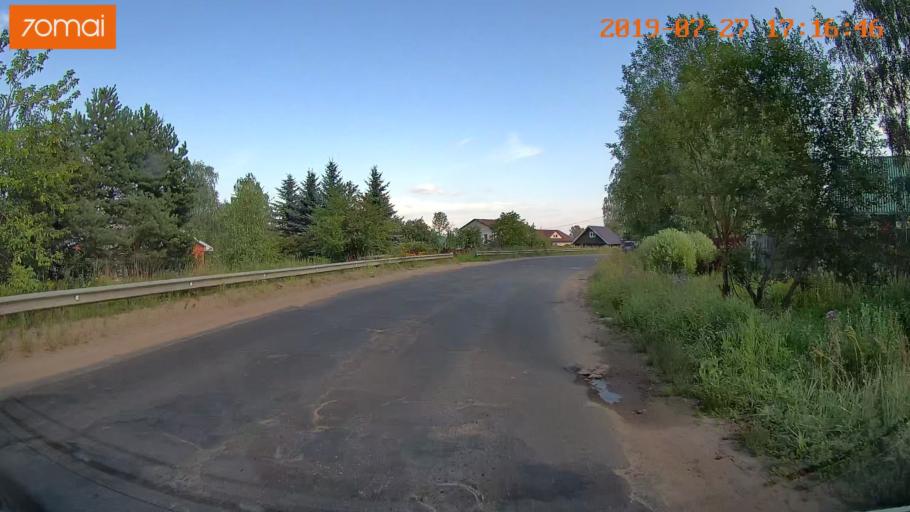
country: RU
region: Ivanovo
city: Novo-Talitsy
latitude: 57.0429
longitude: 40.8896
